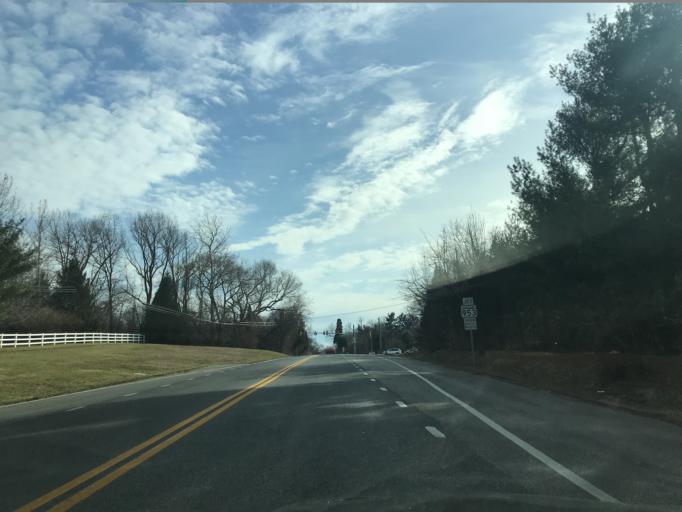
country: US
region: Maryland
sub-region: Prince George's County
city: Woodmore
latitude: 38.9508
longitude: -76.7989
